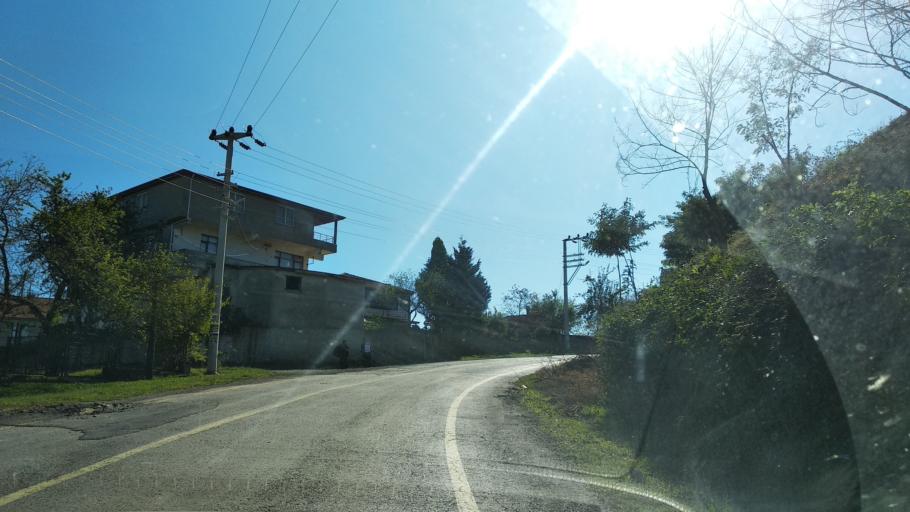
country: TR
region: Sakarya
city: Karasu
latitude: 41.1060
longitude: 30.6395
